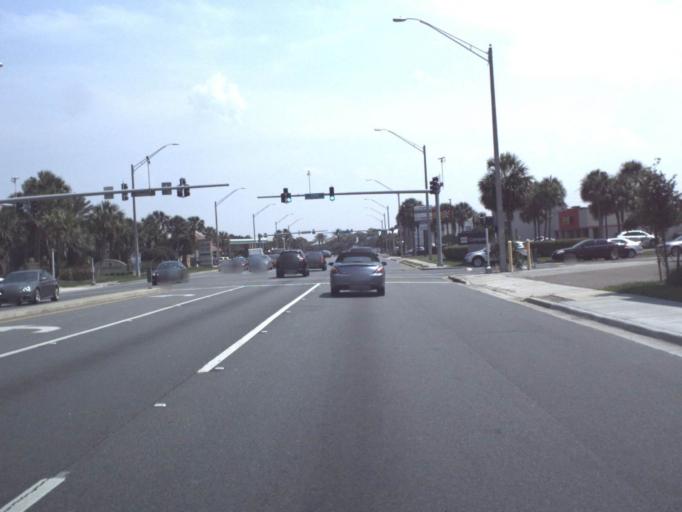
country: US
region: Florida
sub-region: Duval County
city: Jacksonville Beach
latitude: 30.2697
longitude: -81.3886
